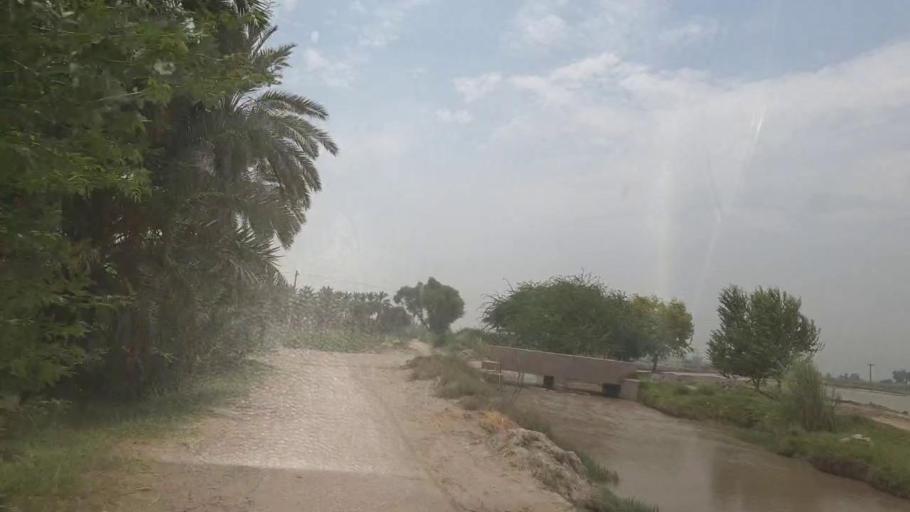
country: PK
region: Sindh
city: Kot Diji
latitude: 27.4420
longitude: 68.6742
